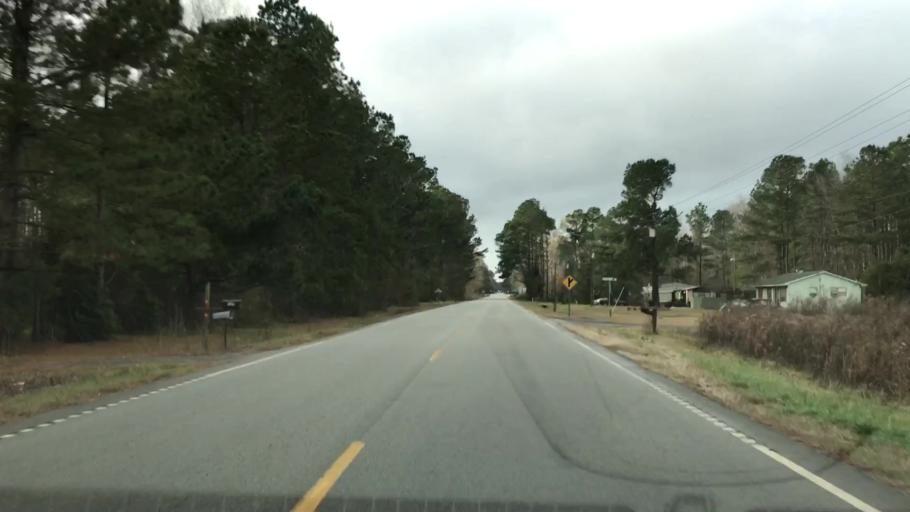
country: US
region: South Carolina
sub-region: Berkeley County
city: Saint Stephen
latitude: 33.2856
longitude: -79.7522
